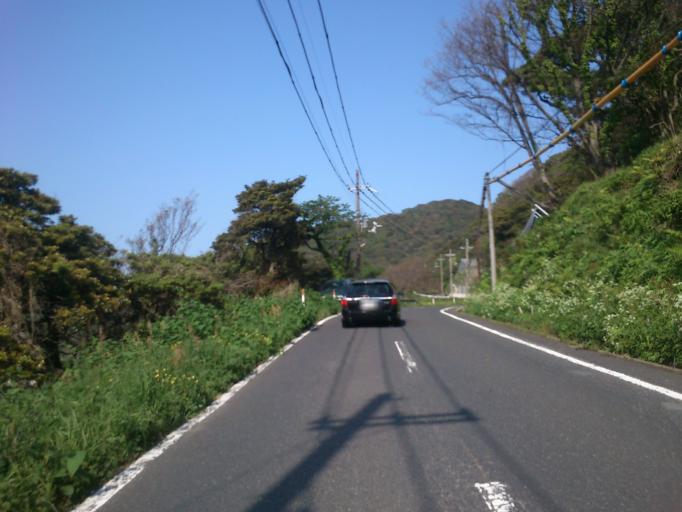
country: JP
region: Kyoto
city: Miyazu
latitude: 35.7684
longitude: 135.2173
